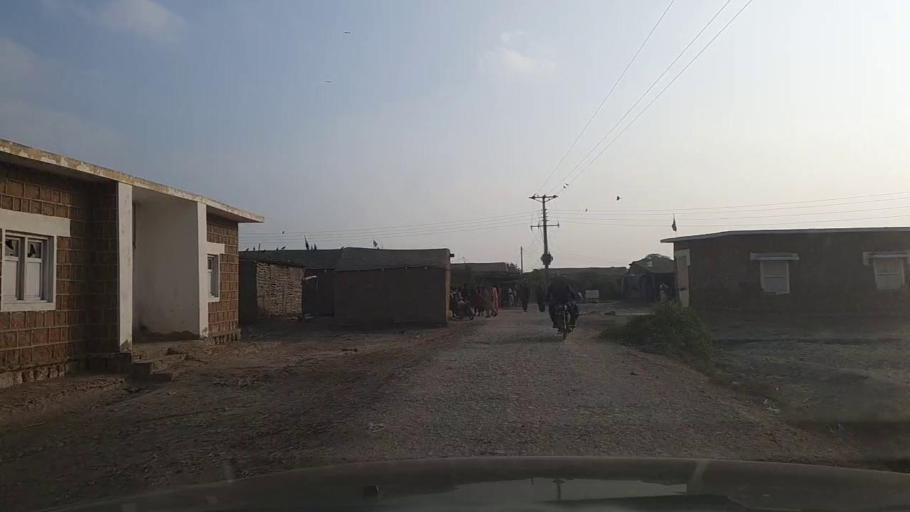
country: PK
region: Sindh
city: Jati
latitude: 24.5370
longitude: 68.3406
